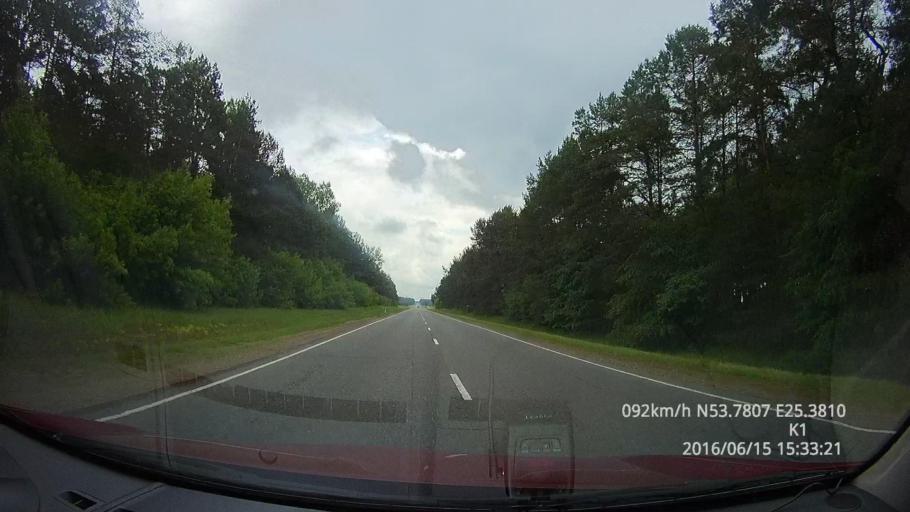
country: BY
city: Berezovka
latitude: 53.7798
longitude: 25.3814
